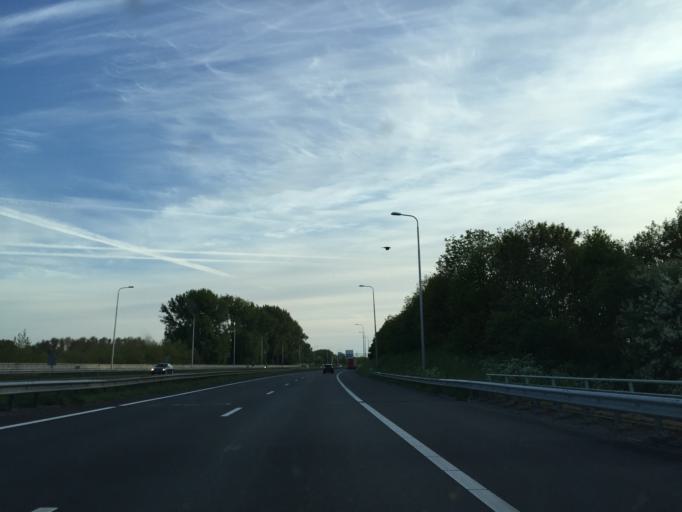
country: NL
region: North Holland
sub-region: Gemeente Hoorn
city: Hoorn
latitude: 52.6435
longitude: 5.0294
